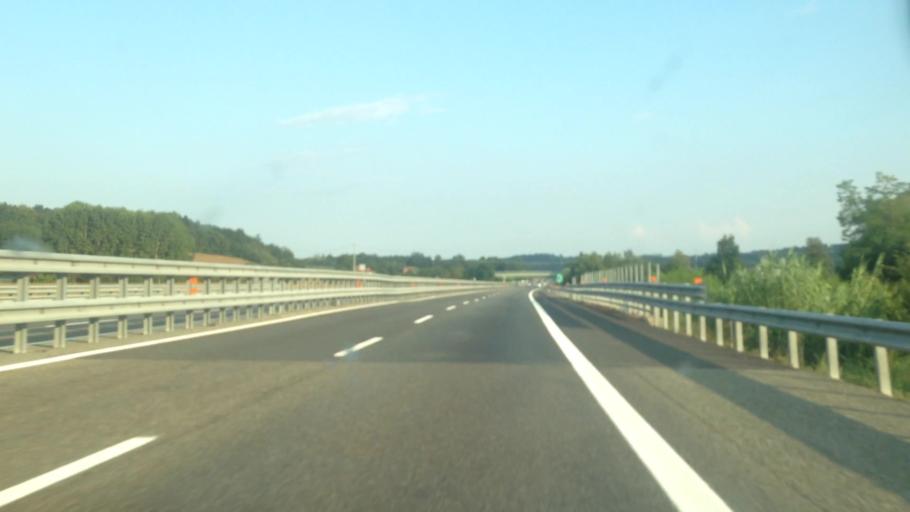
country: IT
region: Piedmont
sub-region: Provincia di Asti
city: Villafranca d'Asti
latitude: 44.9119
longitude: 8.0452
